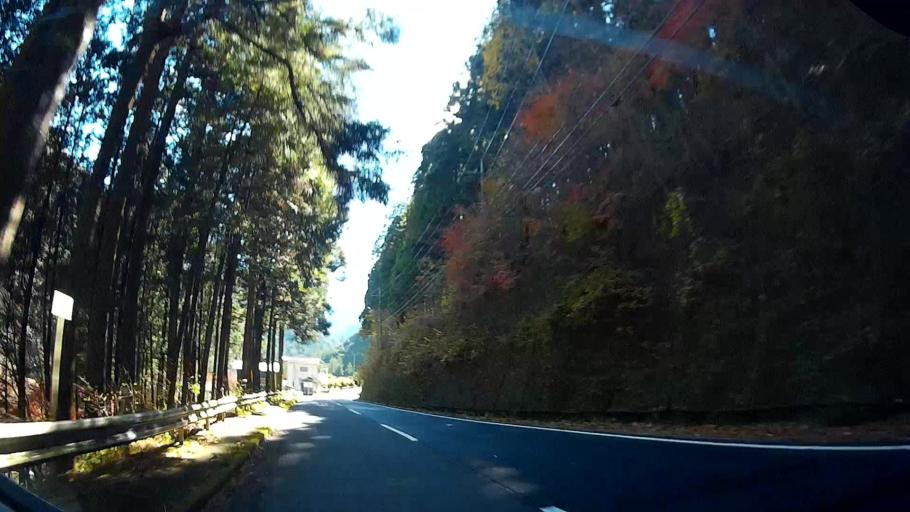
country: JP
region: Tokyo
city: Itsukaichi
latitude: 35.7077
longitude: 139.1527
